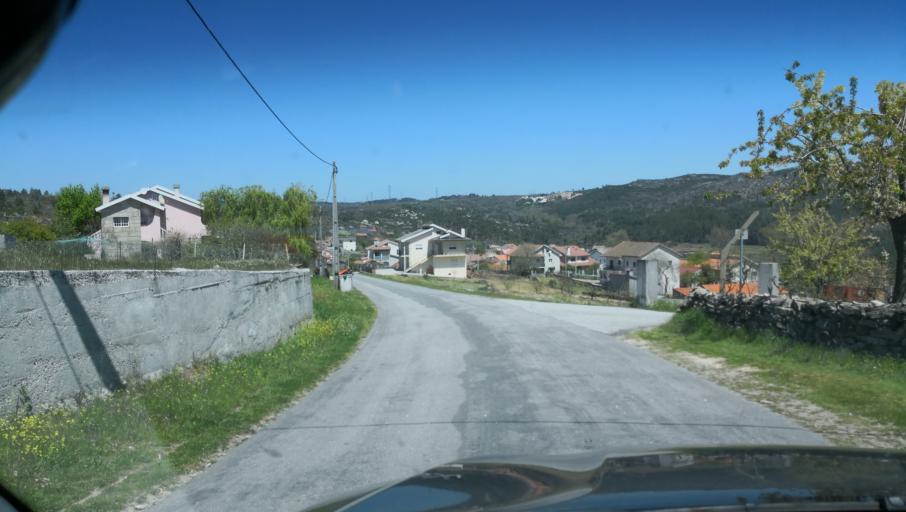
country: PT
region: Vila Real
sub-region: Sabrosa
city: Sabrosa
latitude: 41.2957
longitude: -7.6500
